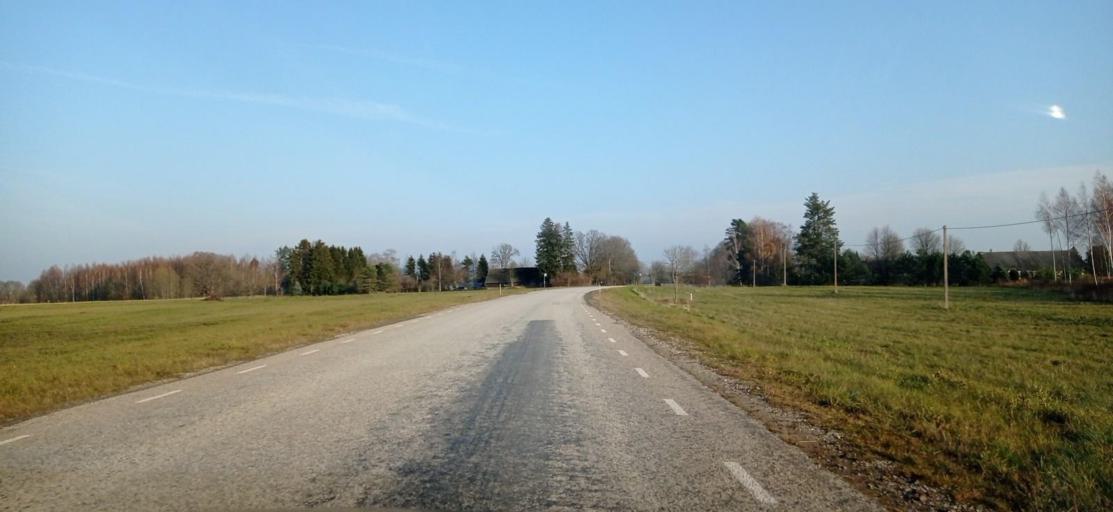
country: EE
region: Jogevamaa
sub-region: Tabivere vald
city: Tabivere
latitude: 58.6816
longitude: 26.6442
